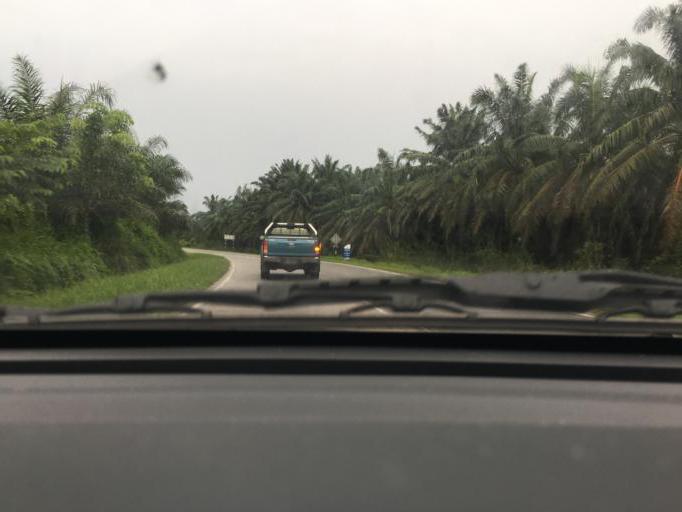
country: MY
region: Kedah
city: Bedong
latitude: 5.6612
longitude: 100.6306
